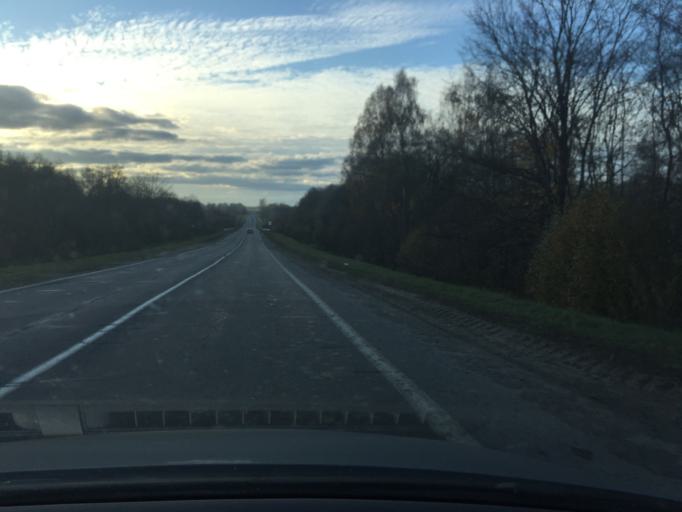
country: BY
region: Vitebsk
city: Vyerkhnyadzvinsk
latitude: 55.8378
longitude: 27.8885
